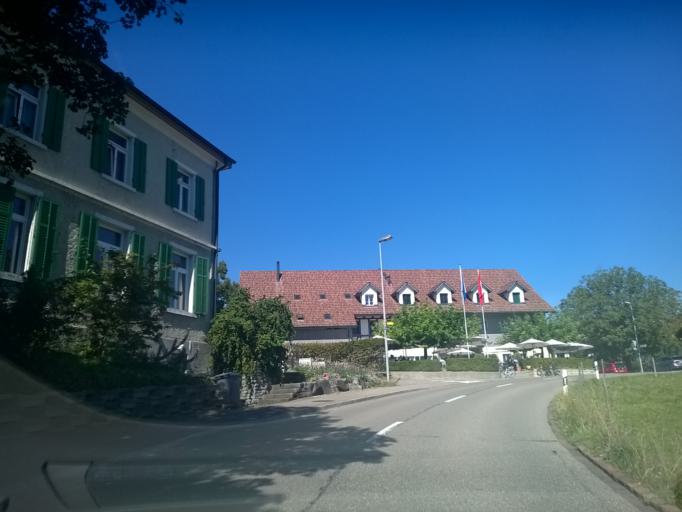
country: CH
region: Zurich
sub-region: Bezirk Buelach
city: Birchwil
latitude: 47.4635
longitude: 8.6396
